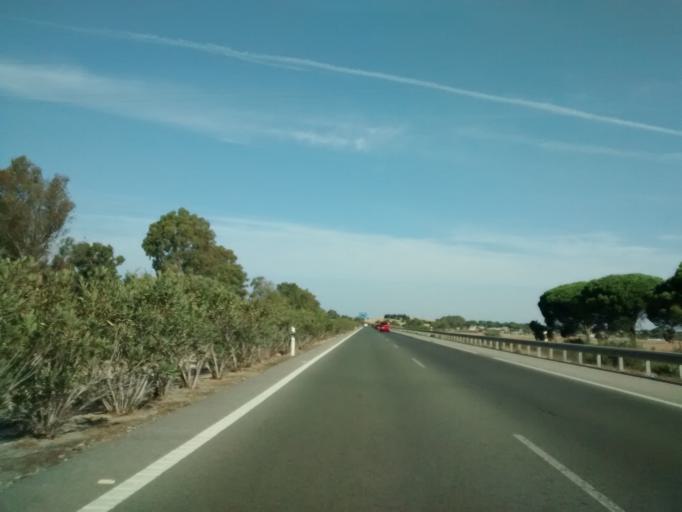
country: ES
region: Andalusia
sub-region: Provincia de Cadiz
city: Chiclana de la Frontera
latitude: 36.3839
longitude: -6.1157
